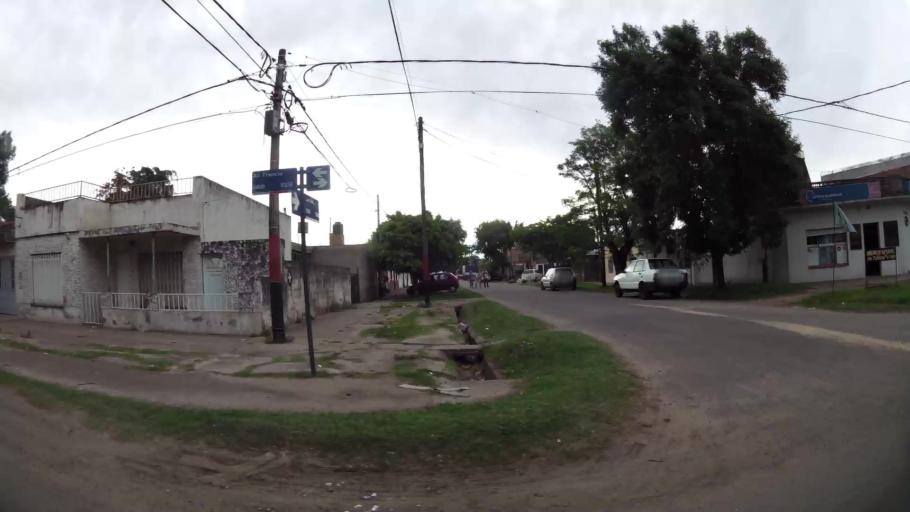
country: AR
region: Santa Fe
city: Gobernador Galvez
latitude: -33.0003
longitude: -60.6779
